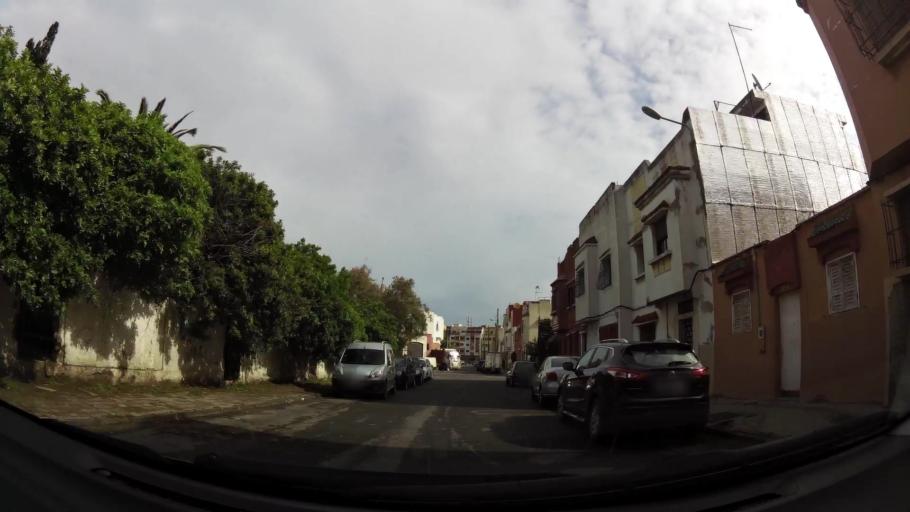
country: MA
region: Grand Casablanca
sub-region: Casablanca
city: Casablanca
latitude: 33.5639
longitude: -7.6698
